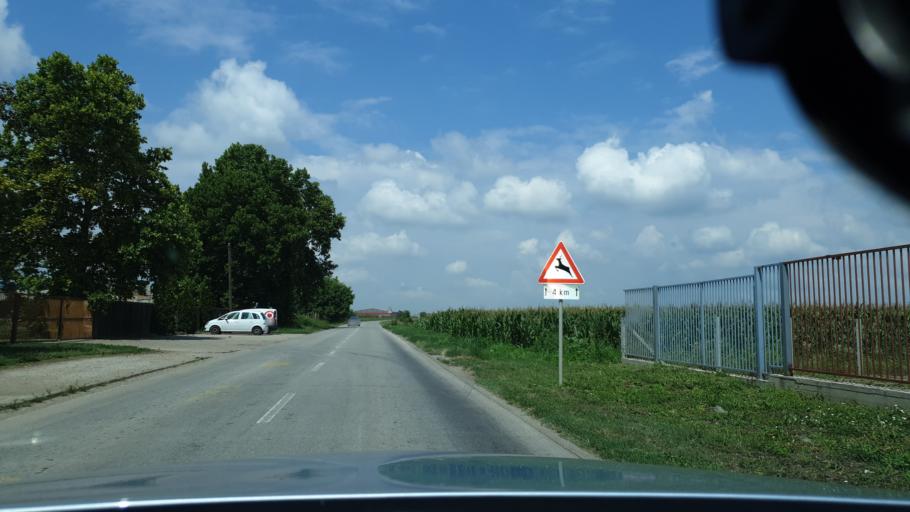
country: RS
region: Autonomna Pokrajina Vojvodina
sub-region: Juznobacki Okrug
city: Kovilj
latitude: 45.2422
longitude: 20.0246
